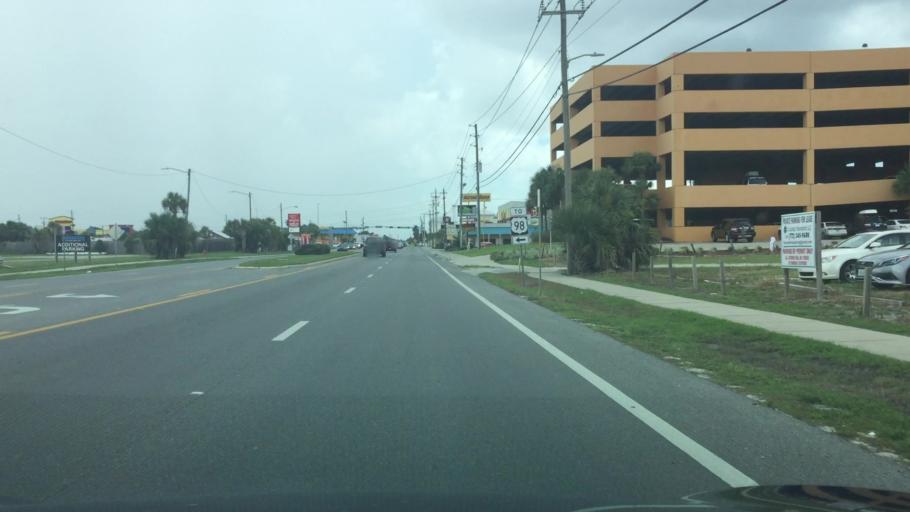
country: US
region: Florida
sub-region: Bay County
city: Lower Grand Lagoon
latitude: 30.1411
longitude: -85.7528
